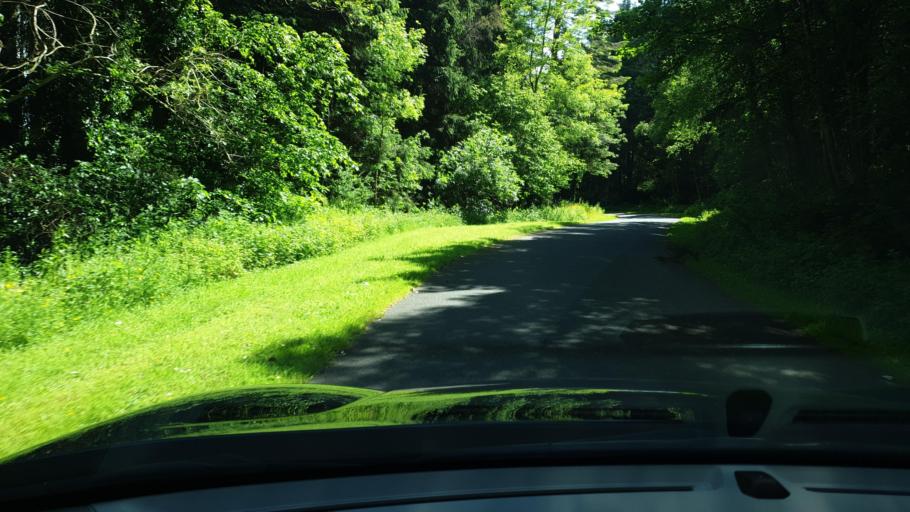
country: IE
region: Ulster
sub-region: An Cabhan
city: Kingscourt
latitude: 53.9145
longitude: -6.7887
